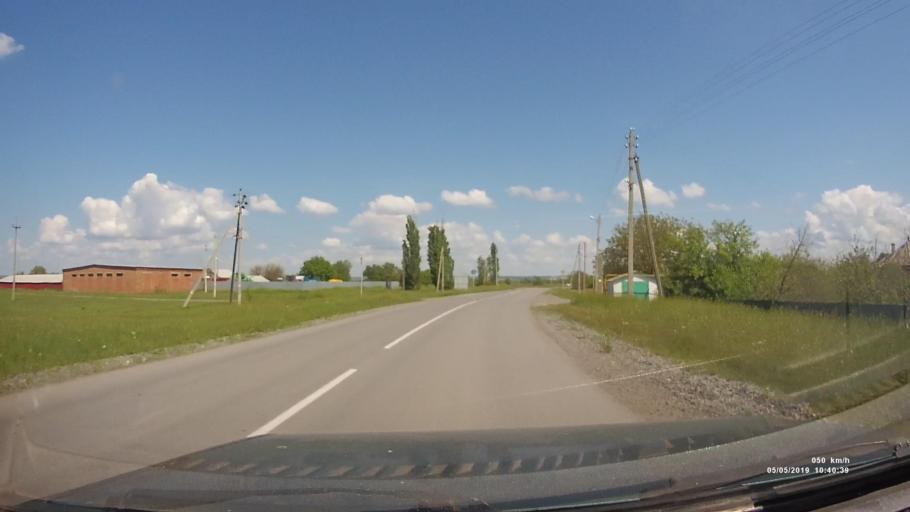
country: RU
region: Rostov
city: Ust'-Donetskiy
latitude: 47.5858
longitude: 40.8420
